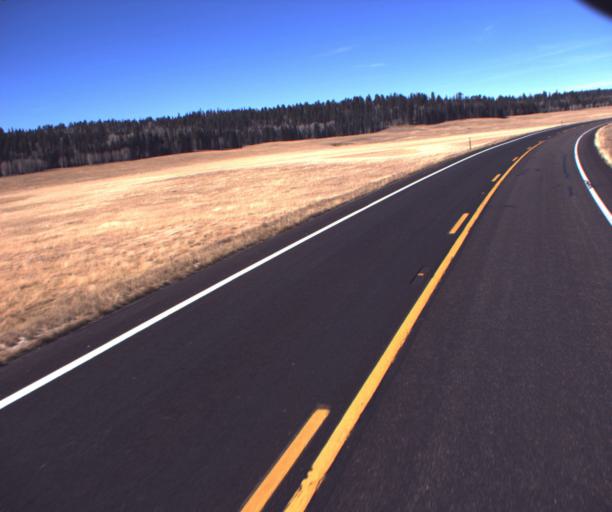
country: US
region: Arizona
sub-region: Coconino County
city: Grand Canyon
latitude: 36.4242
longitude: -112.1306
